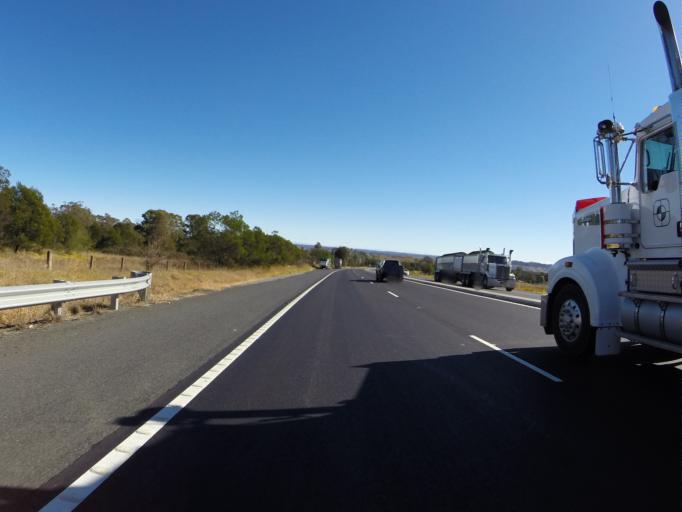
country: AU
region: New South Wales
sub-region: Wollondilly
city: Douglas Park
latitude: -34.2329
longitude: 150.6731
